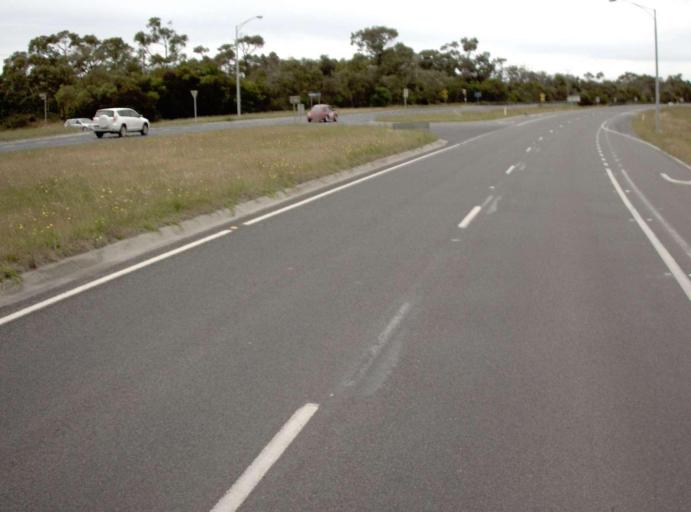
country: AU
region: Victoria
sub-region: Casey
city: Junction Village
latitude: -38.1293
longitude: 145.2919
